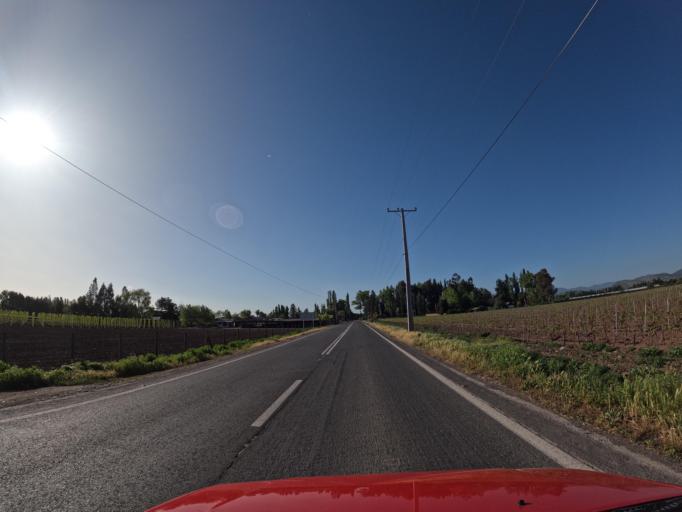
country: CL
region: Maule
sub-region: Provincia de Curico
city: Teno
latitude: -34.7575
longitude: -71.2396
